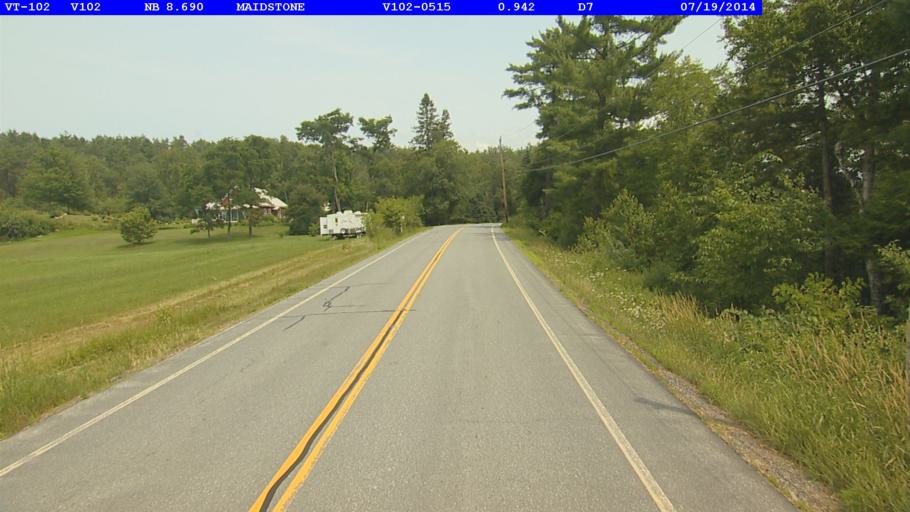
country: US
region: Vermont
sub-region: Essex County
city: Guildhall
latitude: 44.5835
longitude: -71.5536
